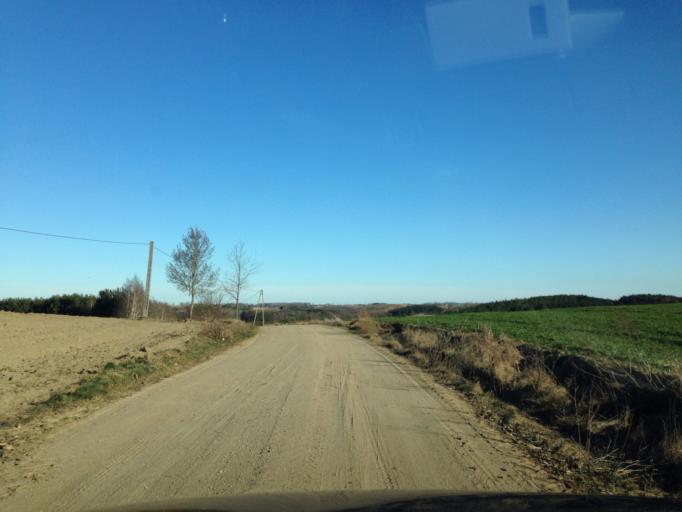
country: PL
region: Kujawsko-Pomorskie
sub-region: Powiat brodnicki
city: Brzozie
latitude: 53.2974
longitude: 19.6592
